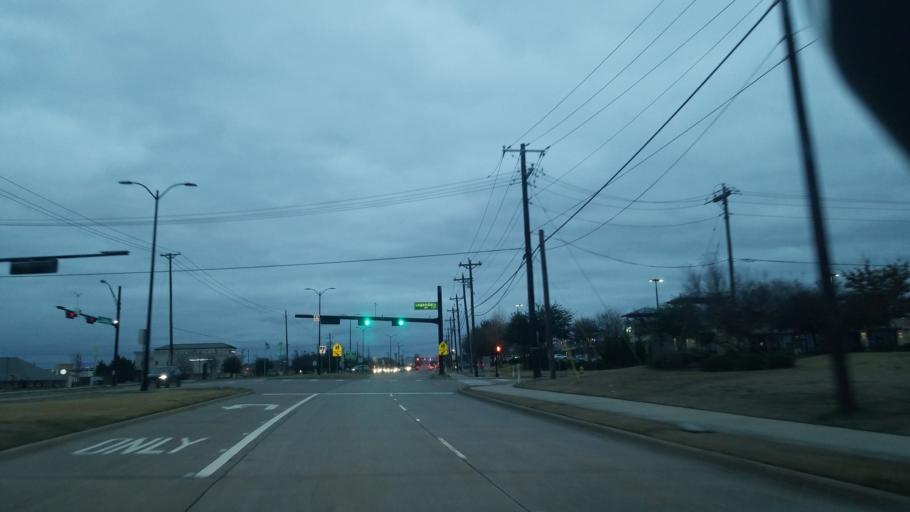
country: US
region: Texas
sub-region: Collin County
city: Frisco
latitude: 33.1229
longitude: -96.8094
